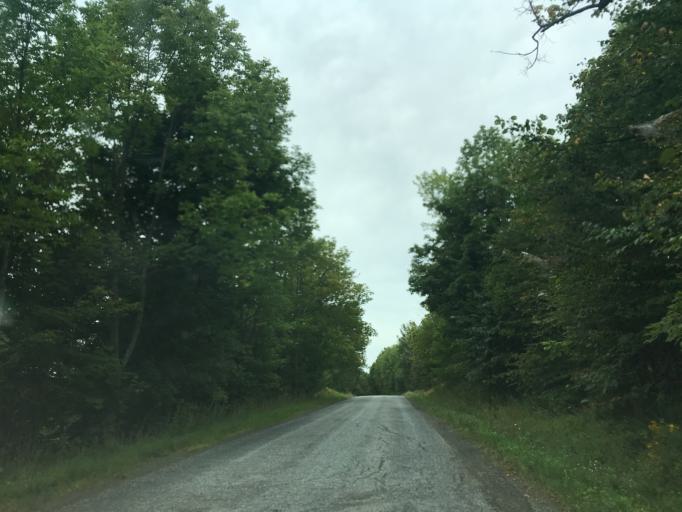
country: US
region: New York
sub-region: Otsego County
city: Worcester
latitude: 42.5914
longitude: -74.6955
